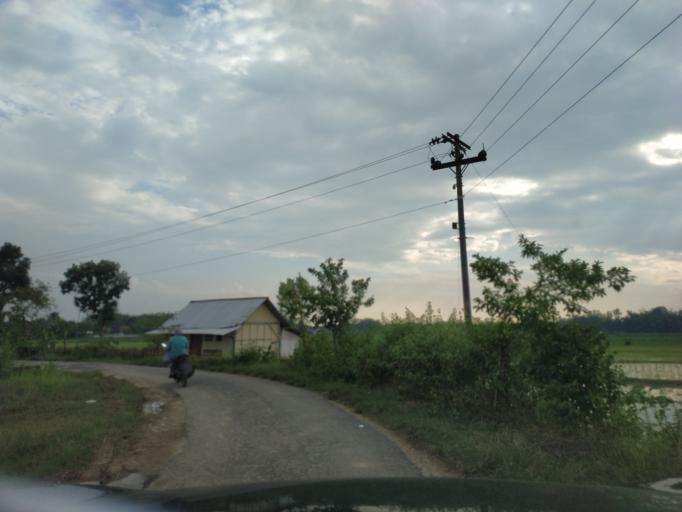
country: ID
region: Central Java
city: Tempuran
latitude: -6.9122
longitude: 111.4558
